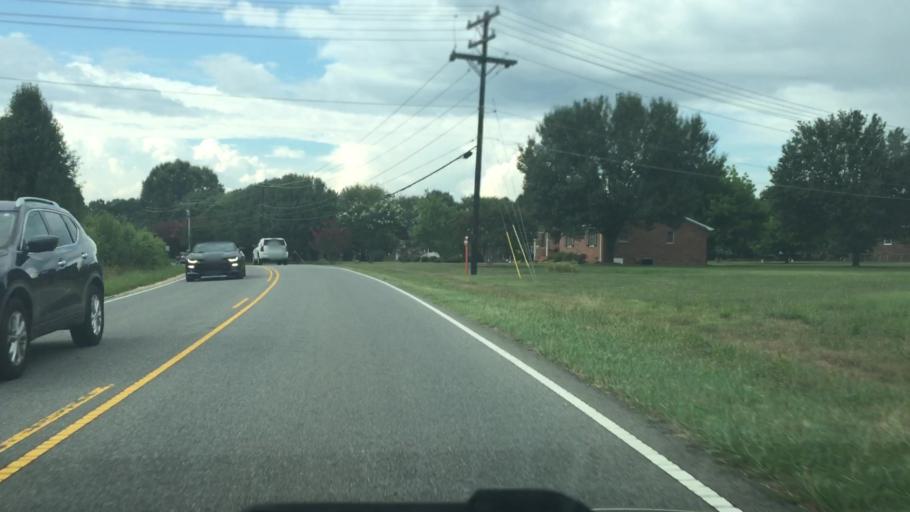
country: US
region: North Carolina
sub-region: Cabarrus County
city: Harrisburg
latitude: 35.4205
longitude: -80.7091
